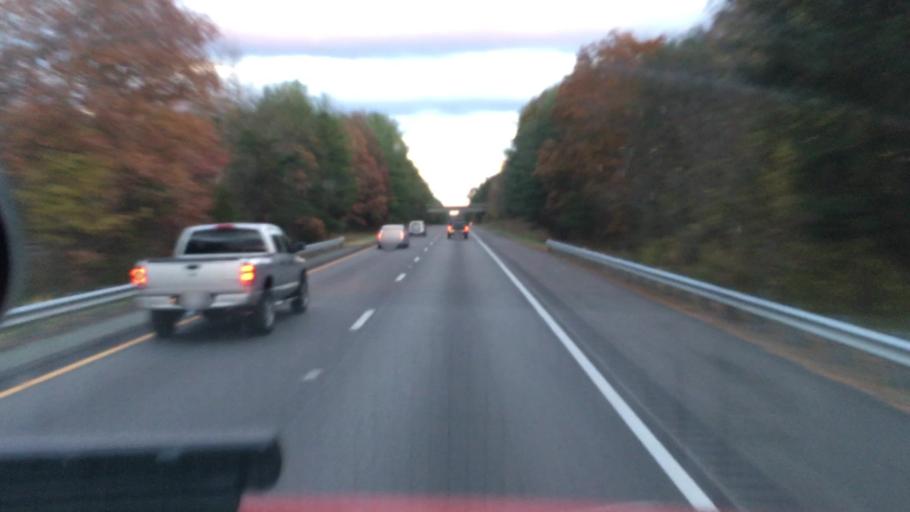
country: US
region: Virginia
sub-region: Fluvanna County
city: Palmyra
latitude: 37.9592
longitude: -78.1678
